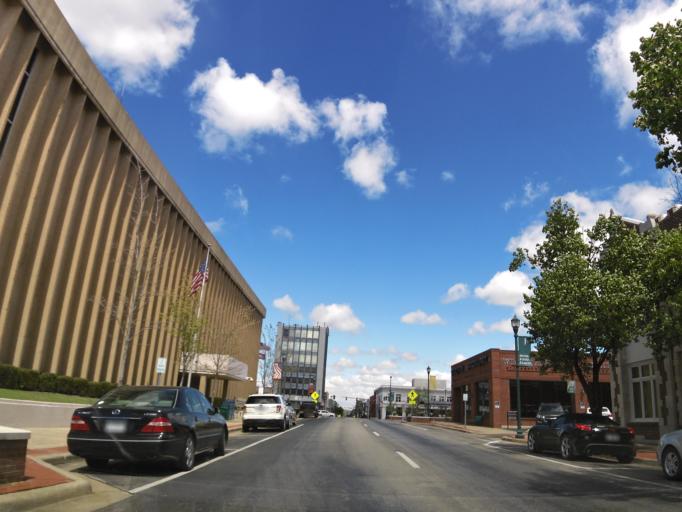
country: US
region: Arkansas
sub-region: Craighead County
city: Jonesboro
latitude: 35.8371
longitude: -90.7053
